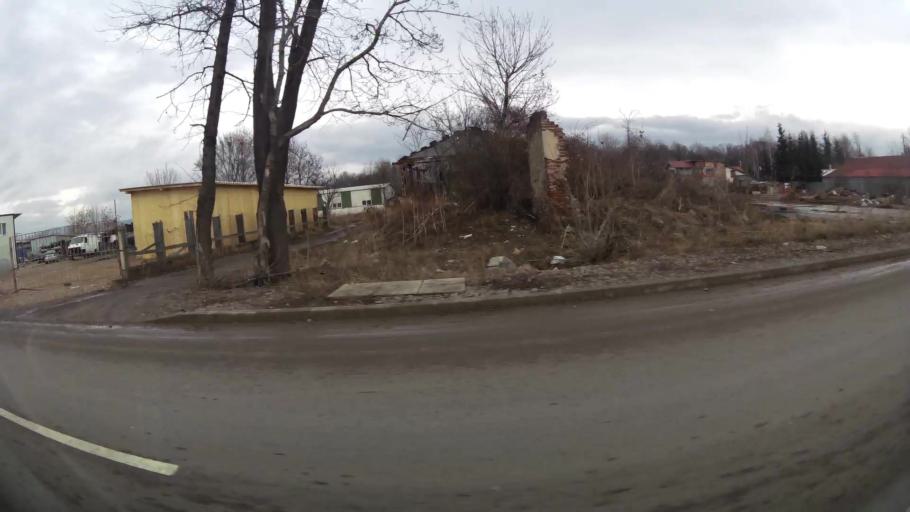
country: BG
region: Sofiya
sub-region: Obshtina Bozhurishte
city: Bozhurishte
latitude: 42.7585
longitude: 23.2683
